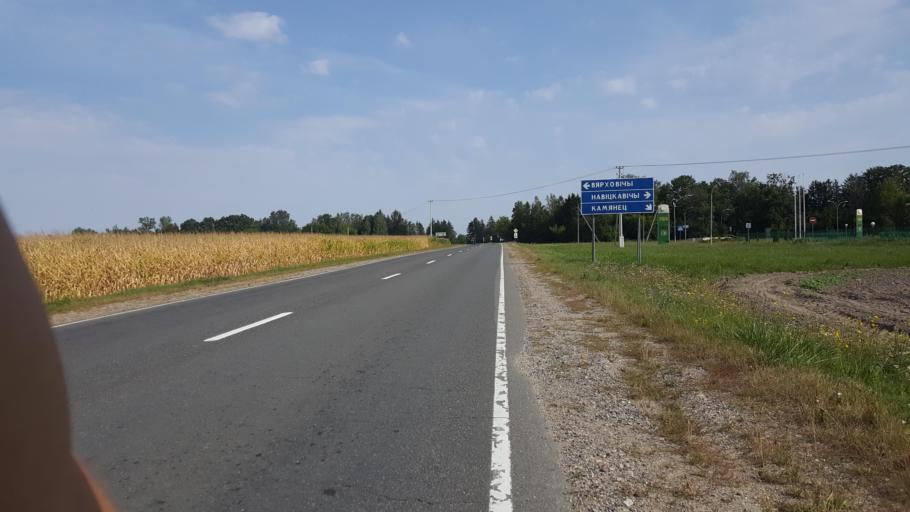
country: BY
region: Brest
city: Kamyanyets
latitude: 52.4097
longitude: 23.7870
